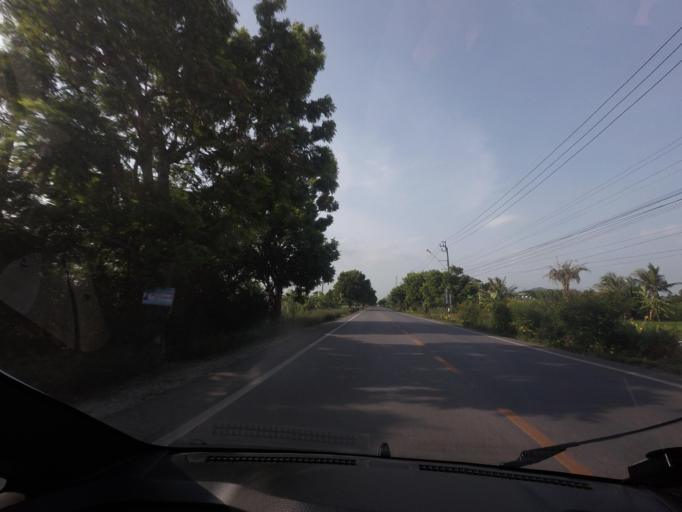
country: TH
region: Bangkok
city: Lat Krabang
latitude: 13.7360
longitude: 100.8622
